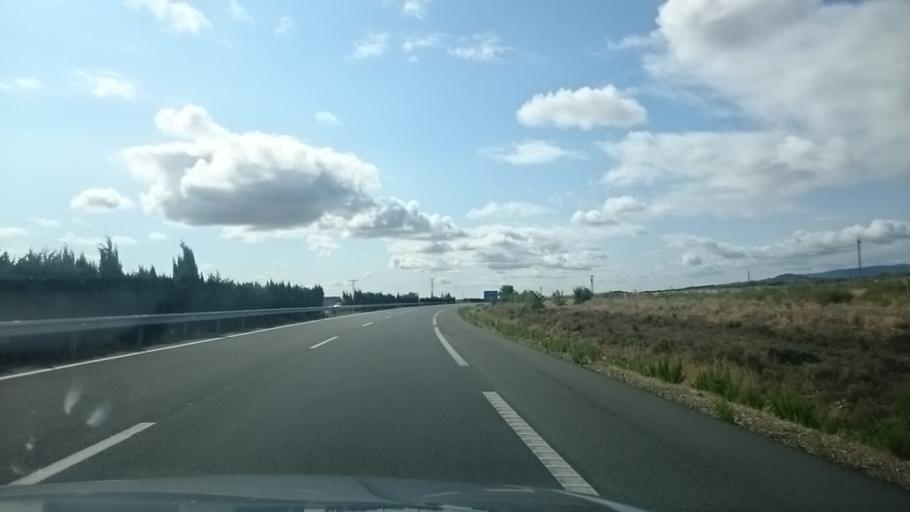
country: ES
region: La Rioja
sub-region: Provincia de La Rioja
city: Calahorra
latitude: 42.3196
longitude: -1.9892
